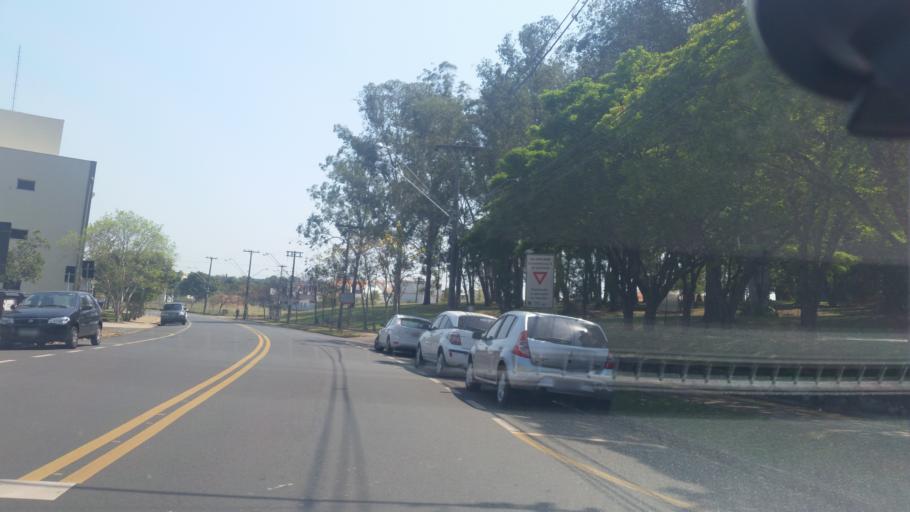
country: BR
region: Sao Paulo
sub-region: Campinas
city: Campinas
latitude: -22.8158
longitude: -47.0664
